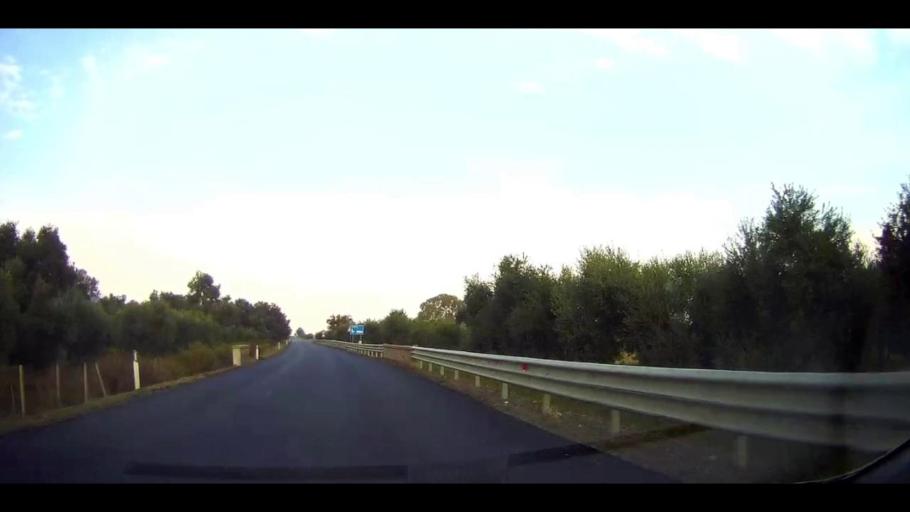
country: IT
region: Calabria
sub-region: Provincia di Crotone
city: Torretta
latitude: 39.4704
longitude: 17.0178
